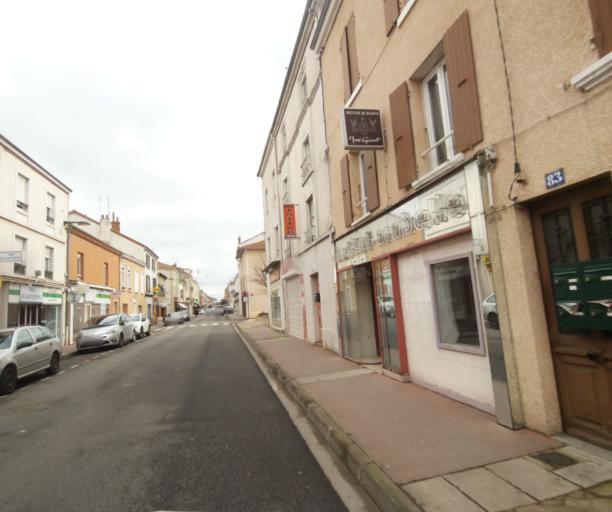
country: FR
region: Rhone-Alpes
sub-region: Departement de la Loire
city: Riorges
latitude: 46.0391
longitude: 4.0562
